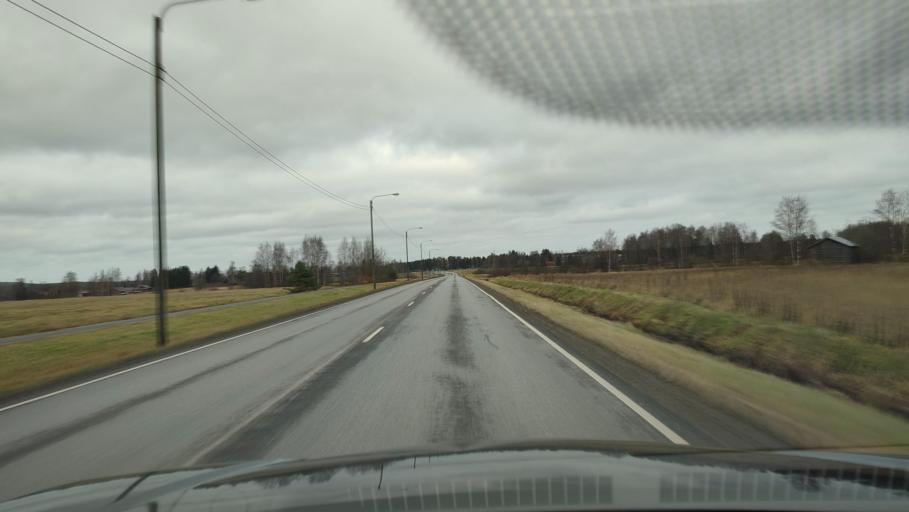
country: FI
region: Southern Ostrobothnia
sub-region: Seinaejoki
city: Kurikka
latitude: 62.6090
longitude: 22.4209
